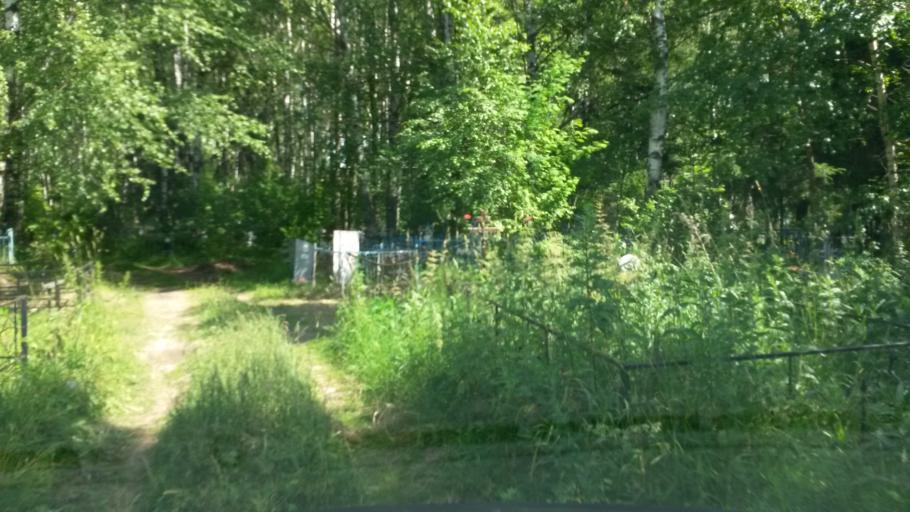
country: RU
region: Ivanovo
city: Zarechnyy
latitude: 57.4722
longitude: 42.3282
